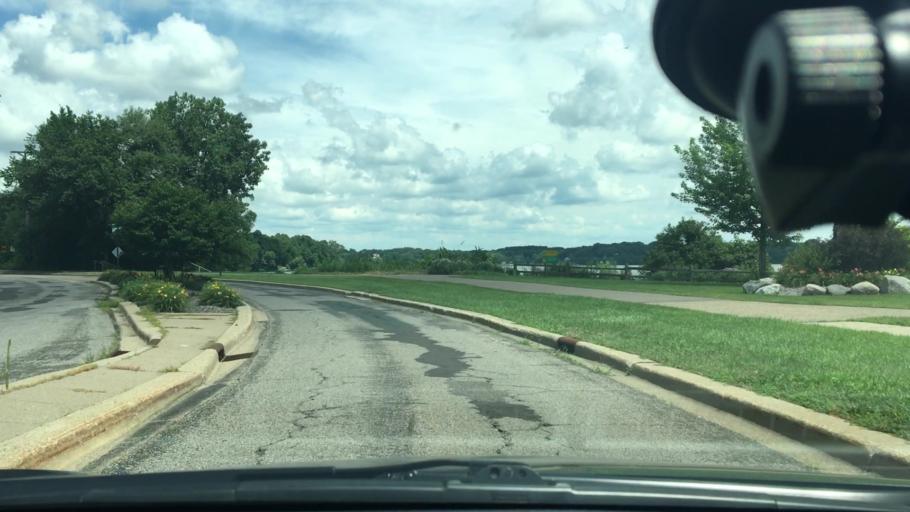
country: US
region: Minnesota
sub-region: Hennepin County
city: Plymouth
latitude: 45.0029
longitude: -93.4306
